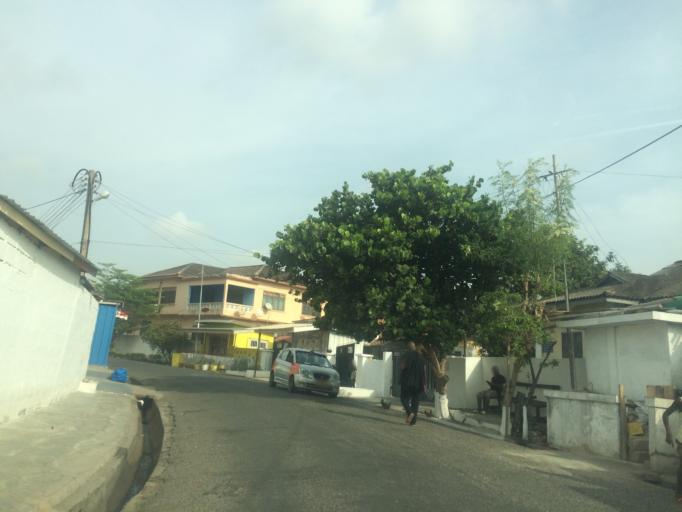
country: GH
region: Greater Accra
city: Accra
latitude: 5.5564
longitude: -0.1791
